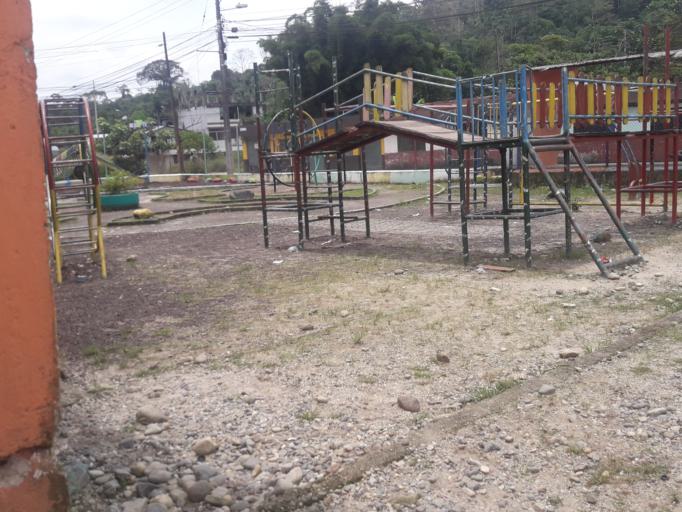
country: EC
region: Napo
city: Tena
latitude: -0.9940
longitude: -77.8089
